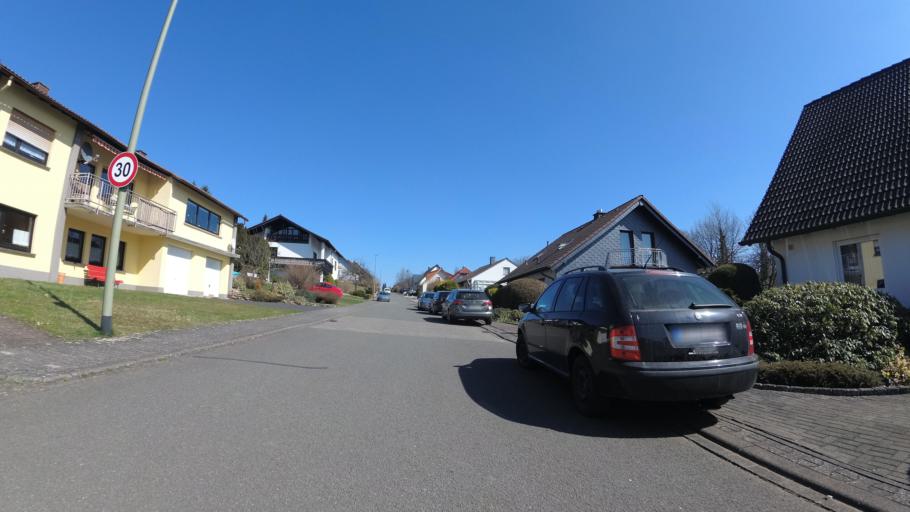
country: DE
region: Rheinland-Pfalz
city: Brucken
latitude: 49.6394
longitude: 7.1202
